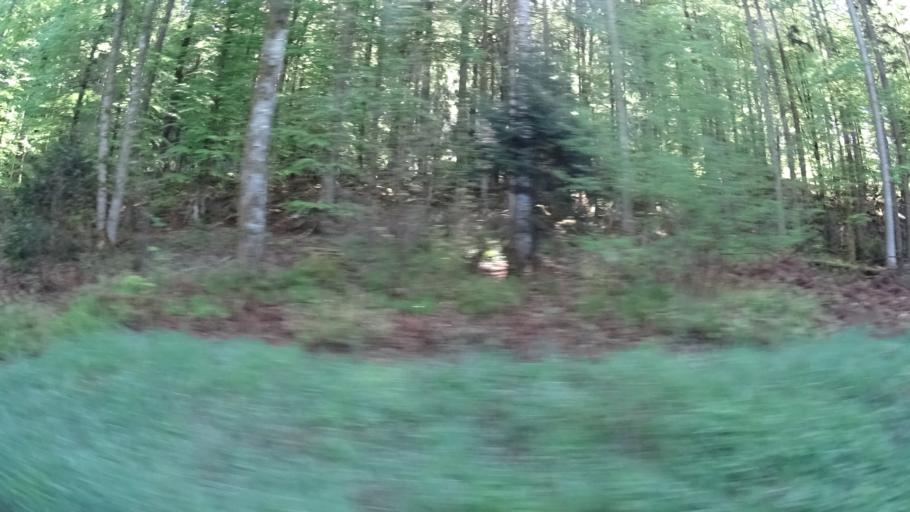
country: DE
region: Baden-Wuerttemberg
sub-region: Karlsruhe Region
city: Bad Wildbad
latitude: 48.7403
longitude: 8.5784
